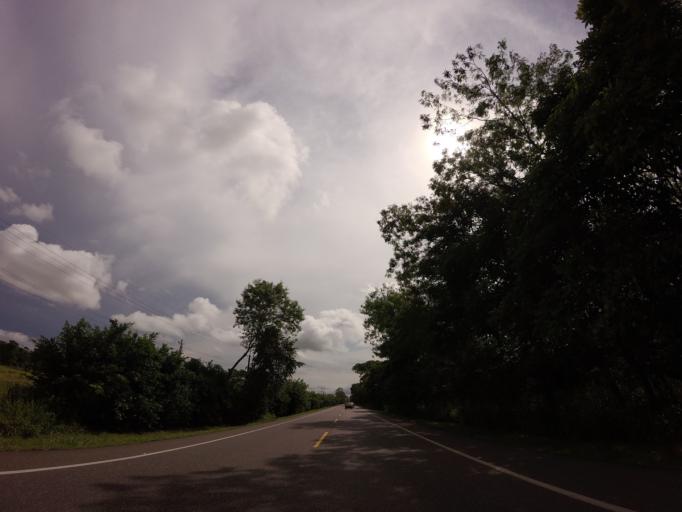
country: CO
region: Caldas
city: La Dorada
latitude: 5.3548
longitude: -74.7280
